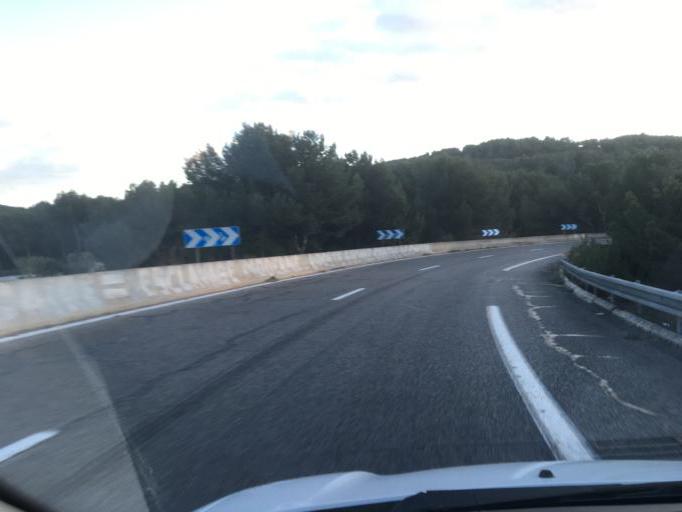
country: FR
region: Provence-Alpes-Cote d'Azur
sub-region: Departement des Bouches-du-Rhone
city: Martigues
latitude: 43.3978
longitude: 5.0458
